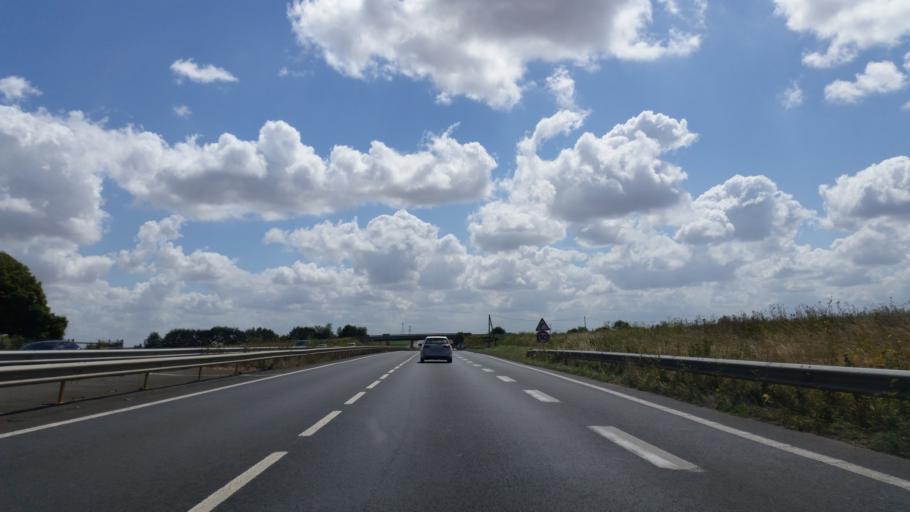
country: FR
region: Lower Normandy
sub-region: Departement du Calvados
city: Ifs
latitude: 49.1250
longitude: -0.3273
